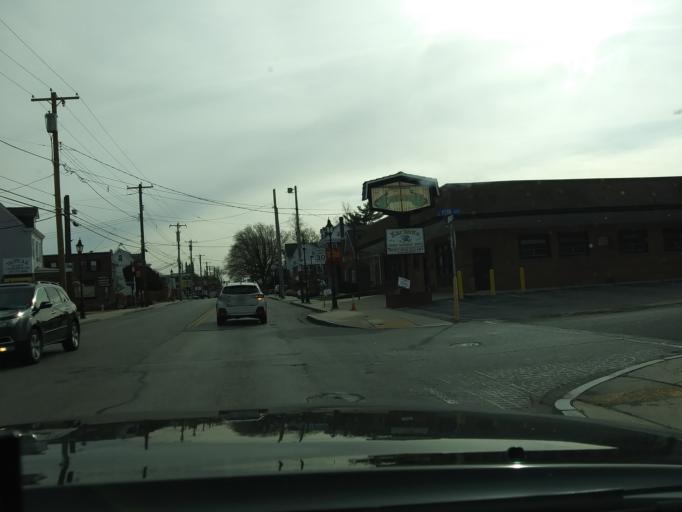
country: US
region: Pennsylvania
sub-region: Montgomery County
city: Rockledge
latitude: 40.0837
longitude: -75.0927
